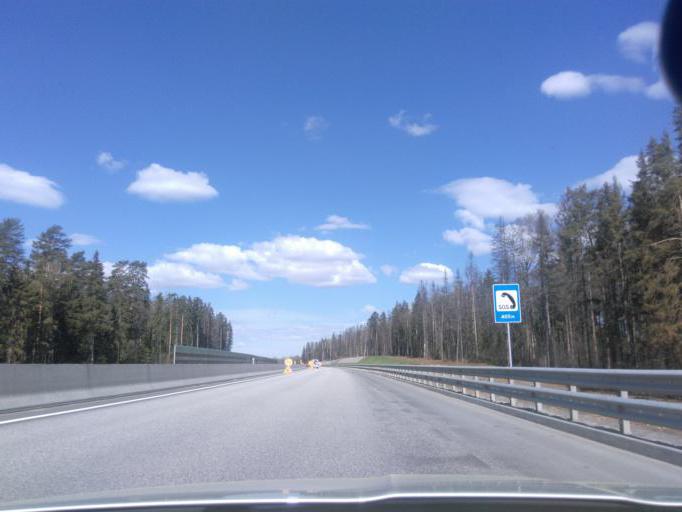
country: RU
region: Moskovskaya
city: Radumlya
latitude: 56.0916
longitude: 37.1974
